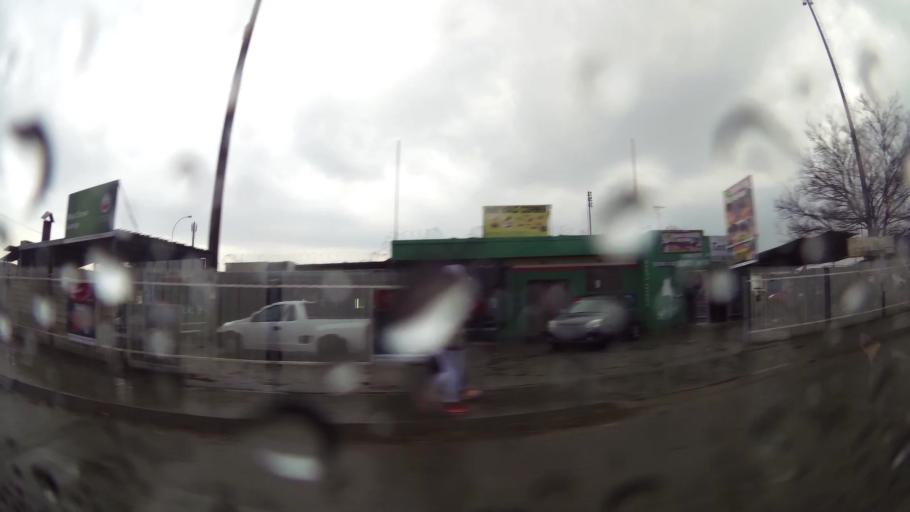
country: ZA
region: Gauteng
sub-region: Ekurhuleni Metropolitan Municipality
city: Germiston
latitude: -26.3539
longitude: 28.1318
